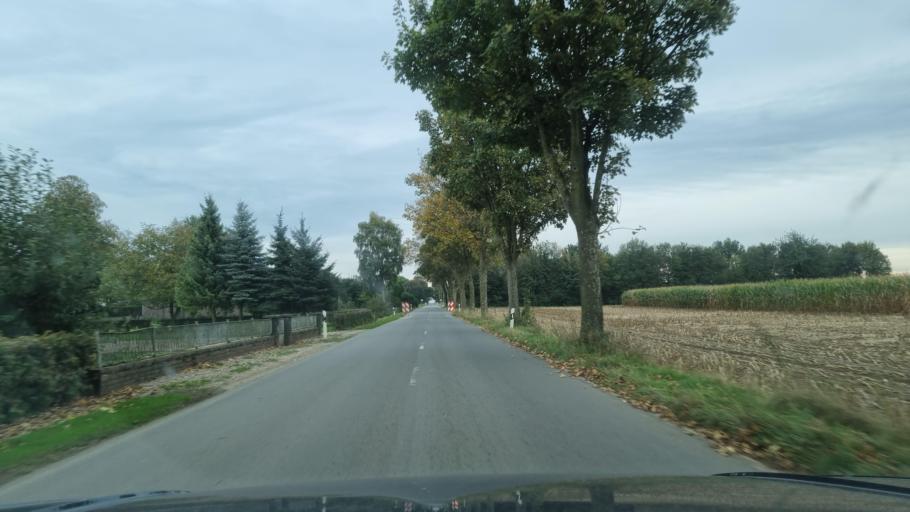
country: DE
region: North Rhine-Westphalia
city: Kalkar
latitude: 51.7104
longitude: 6.2918
